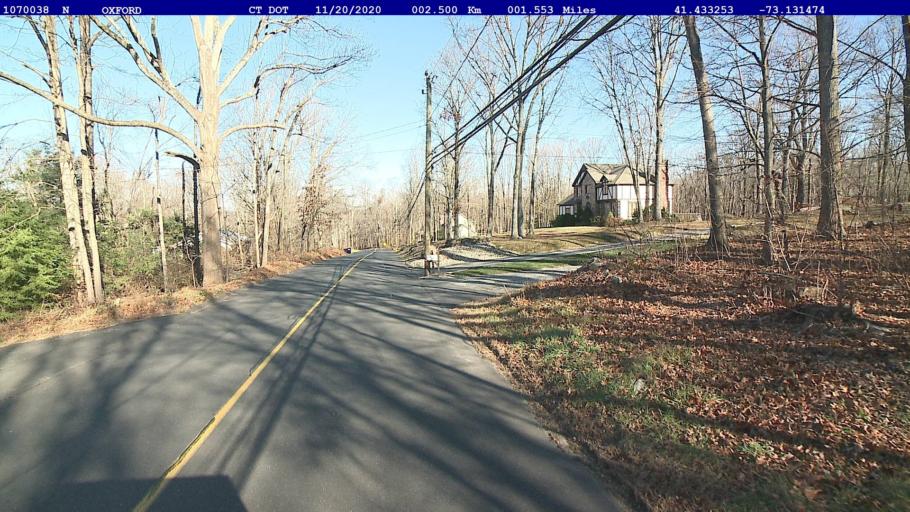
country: US
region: Connecticut
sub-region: New Haven County
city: Oxford
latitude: 41.4333
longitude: -73.1315
